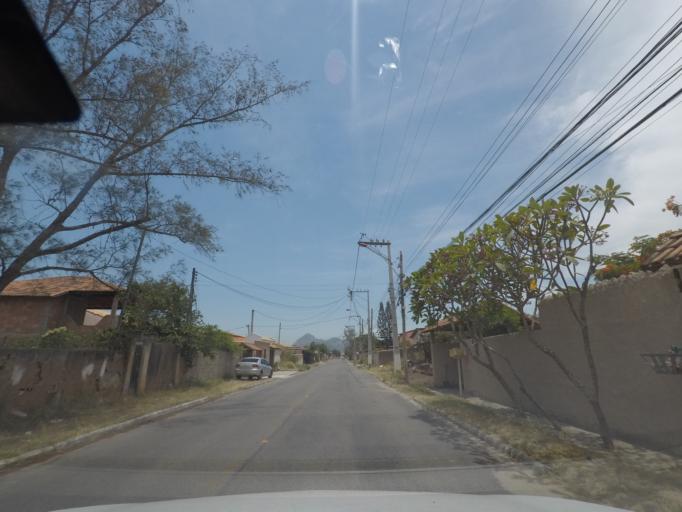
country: BR
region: Rio de Janeiro
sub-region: Marica
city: Marica
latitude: -22.9671
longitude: -42.9551
